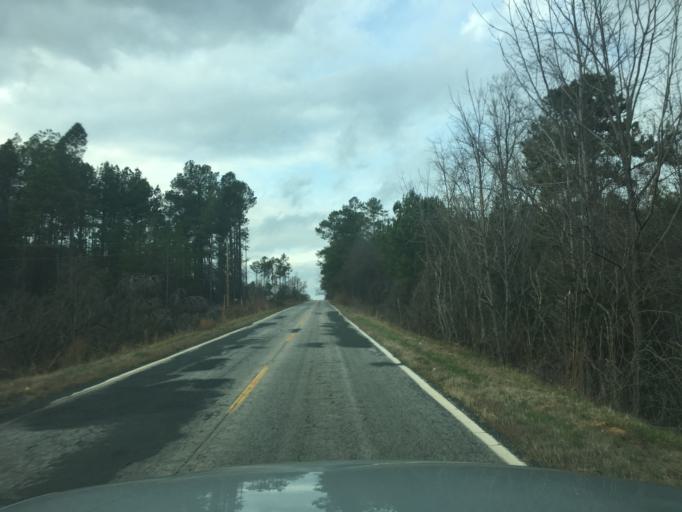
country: US
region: South Carolina
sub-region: Abbeville County
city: Due West
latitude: 34.2773
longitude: -82.4266
